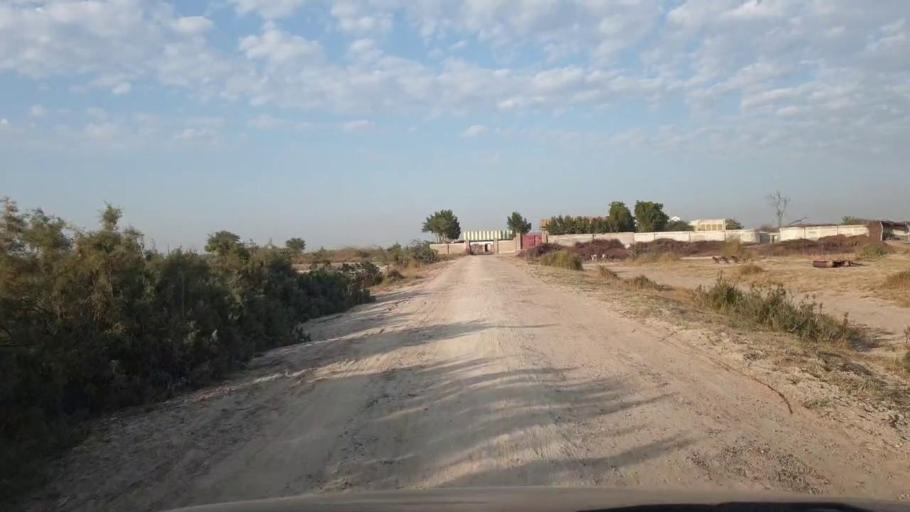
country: PK
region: Sindh
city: Sakrand
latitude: 26.0297
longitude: 68.3842
